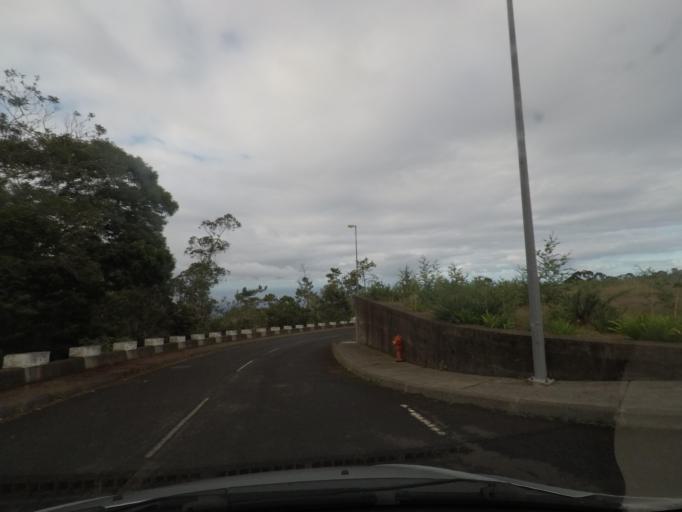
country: PT
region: Madeira
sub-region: Santana
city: Santana
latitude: 32.7873
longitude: -16.8799
